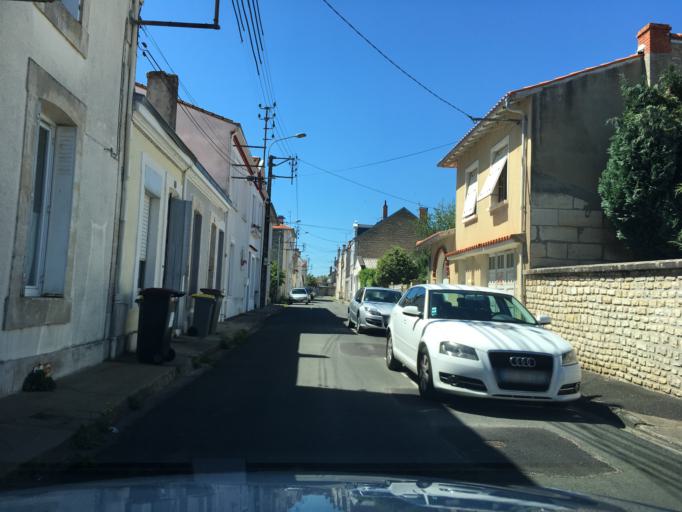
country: FR
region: Poitou-Charentes
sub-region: Departement des Deux-Sevres
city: Niort
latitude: 46.3209
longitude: -0.4492
